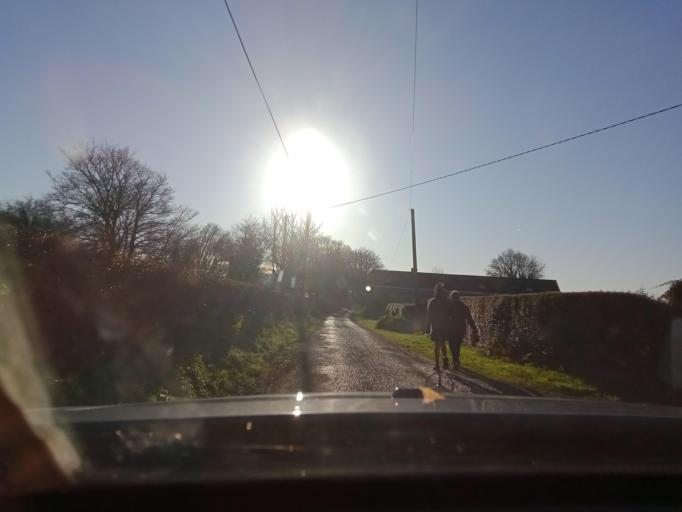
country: IE
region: Munster
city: Carrick-on-Suir
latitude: 52.4374
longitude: -7.4169
